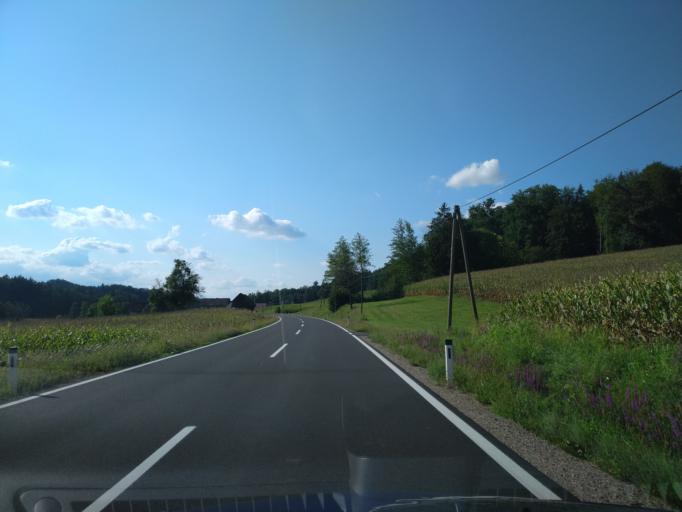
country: AT
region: Styria
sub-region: Politischer Bezirk Leibnitz
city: Sankt Johann im Saggautal
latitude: 46.7250
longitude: 15.4011
